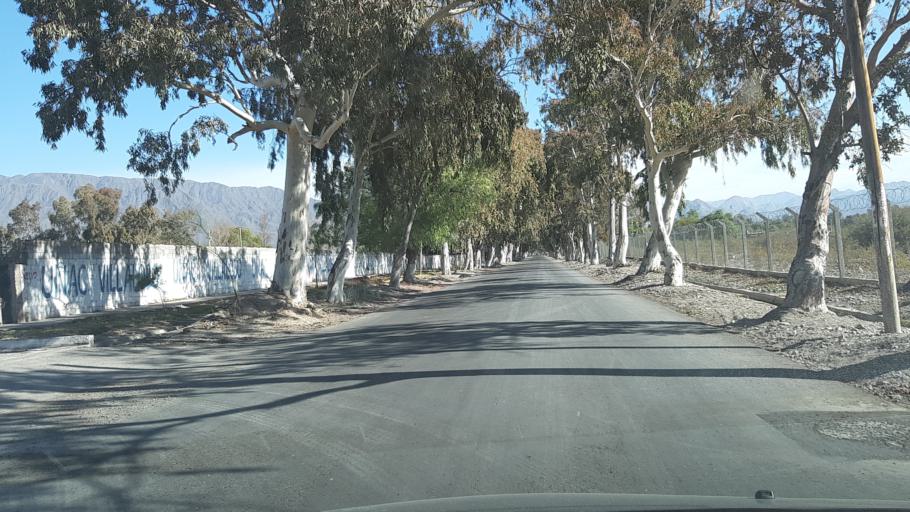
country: AR
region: San Juan
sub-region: Departamento de Zonda
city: Zonda
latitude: -31.5459
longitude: -68.7267
